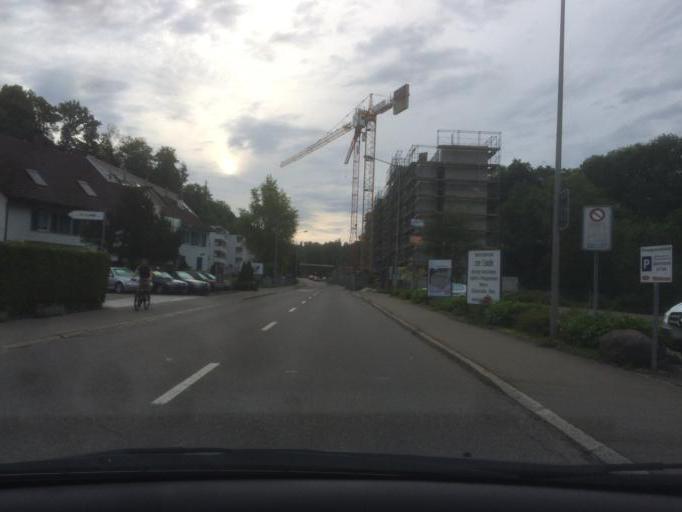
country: CH
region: Zurich
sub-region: Bezirk Uster
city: Uster / Ober-Uster
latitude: 47.3451
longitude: 8.7337
